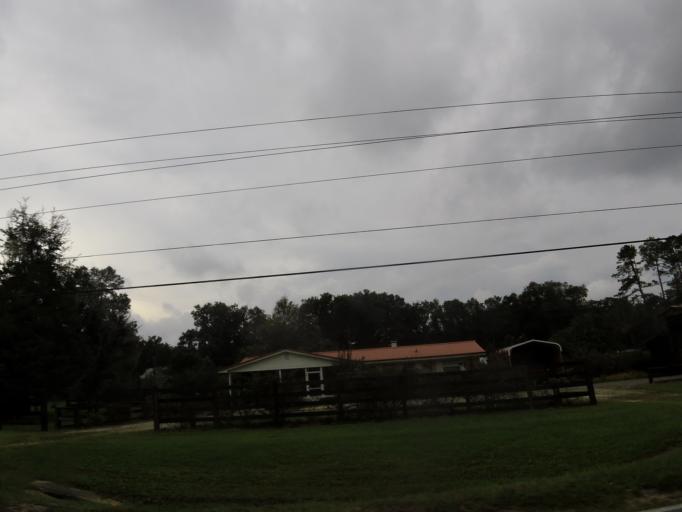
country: US
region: Florida
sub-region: Clay County
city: Middleburg
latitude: 30.1142
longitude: -81.8488
